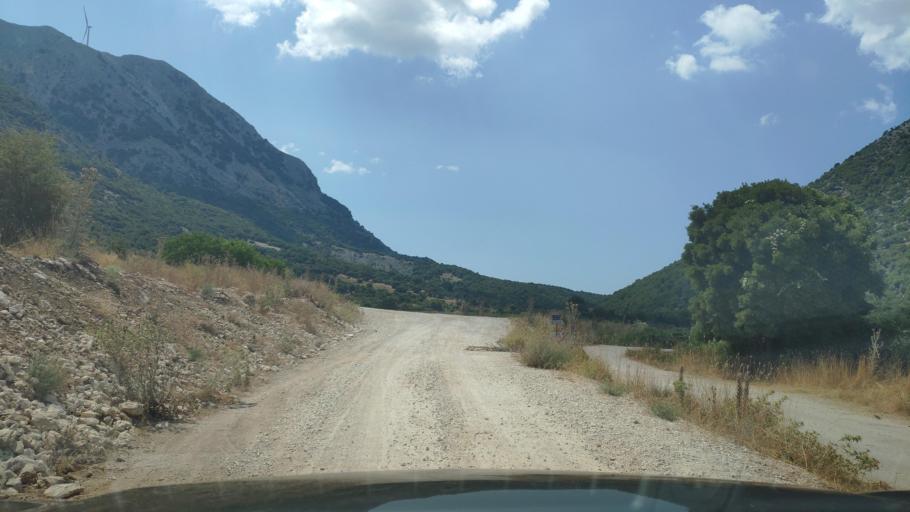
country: GR
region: West Greece
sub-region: Nomos Aitolias kai Akarnanias
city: Kandila
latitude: 38.7768
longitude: 20.9724
